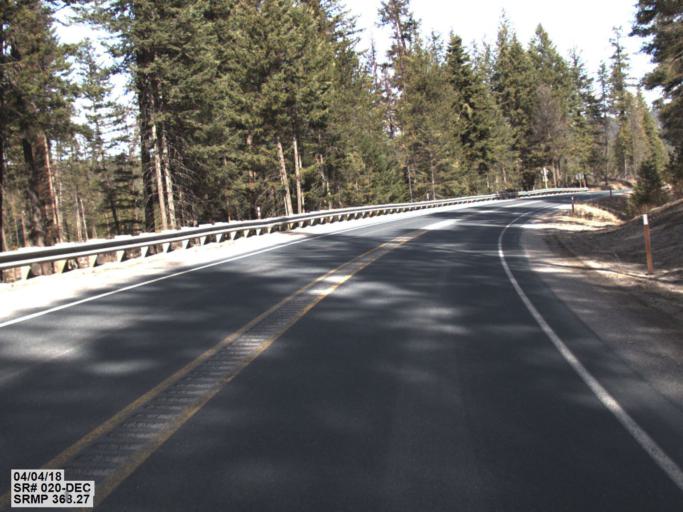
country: US
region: Washington
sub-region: Stevens County
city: Chewelah
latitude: 48.5047
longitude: -117.6724
